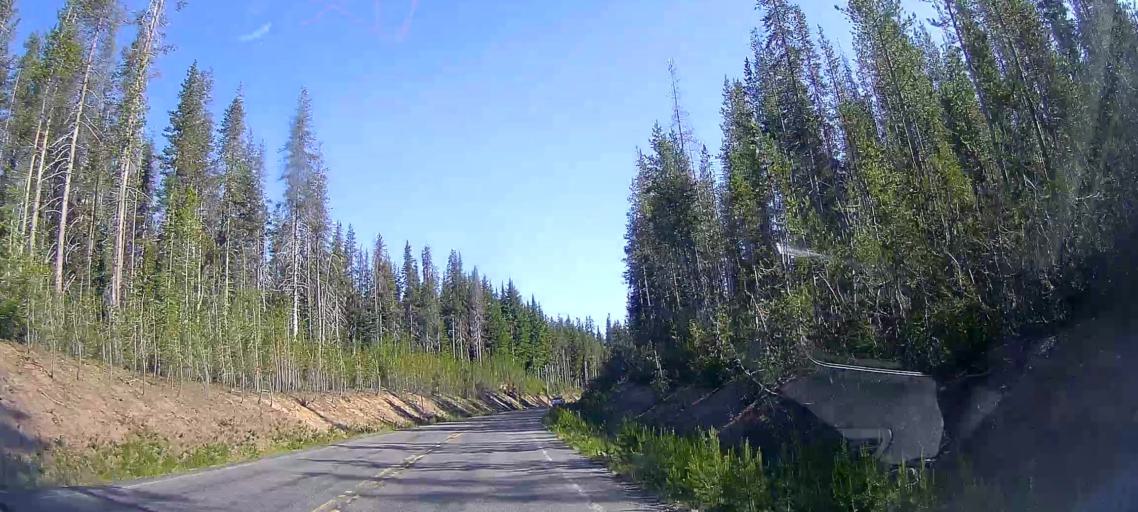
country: US
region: Oregon
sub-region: Jackson County
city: Shady Cove
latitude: 42.8415
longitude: -122.1469
